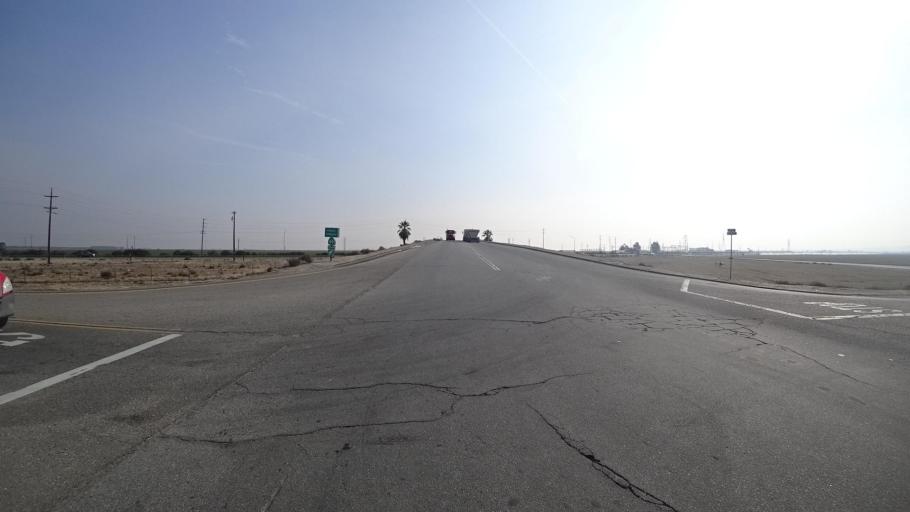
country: US
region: California
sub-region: Kern County
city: Weedpatch
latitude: 35.0952
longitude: -118.9812
